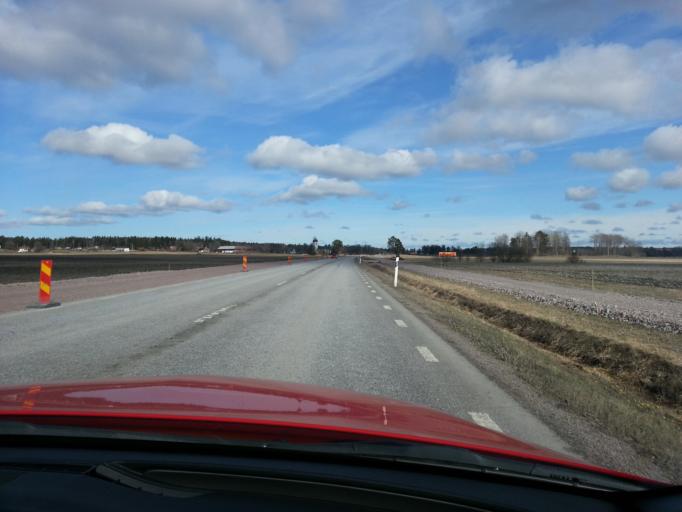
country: SE
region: Uppsala
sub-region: Osthammars Kommun
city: Gimo
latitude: 60.0525
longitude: 18.0557
